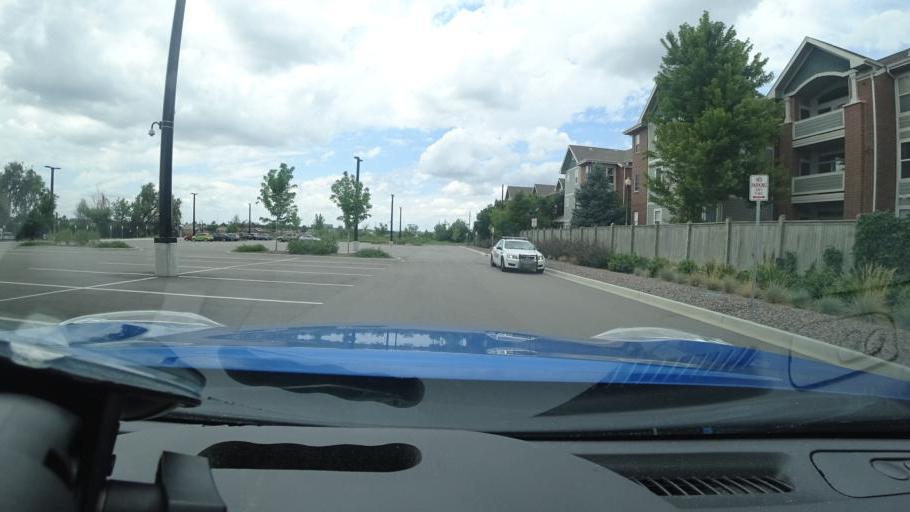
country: US
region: Colorado
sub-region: Adams County
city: Aurora
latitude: 39.7171
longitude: -104.8242
